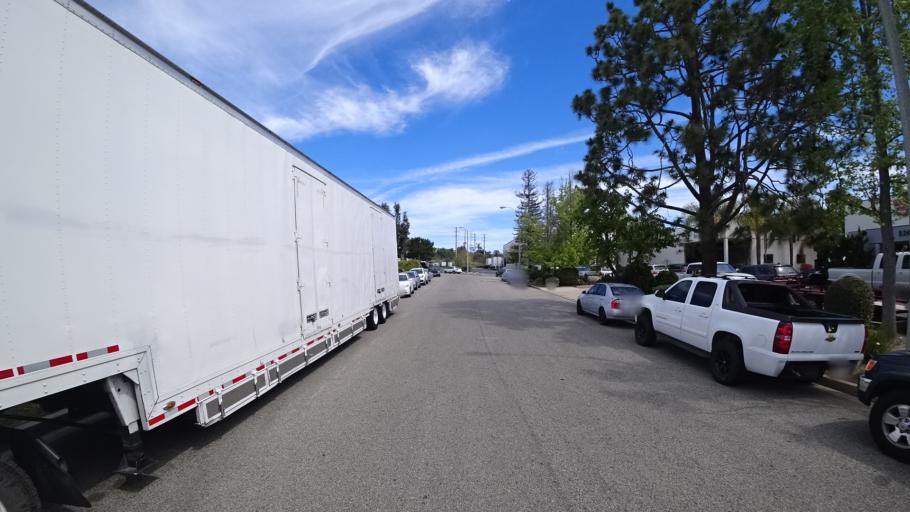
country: US
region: California
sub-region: Ventura County
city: Casa Conejo
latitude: 34.1938
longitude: -118.9315
